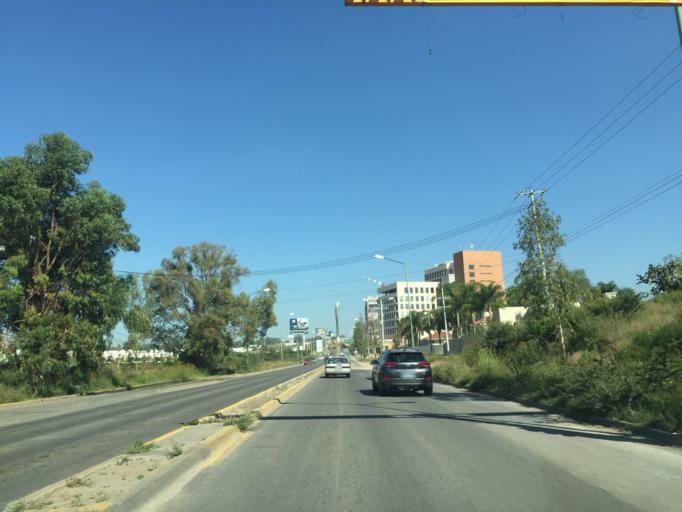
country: MX
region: Guanajuato
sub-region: Leon
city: La Ermita
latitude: 21.1687
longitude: -101.7307
